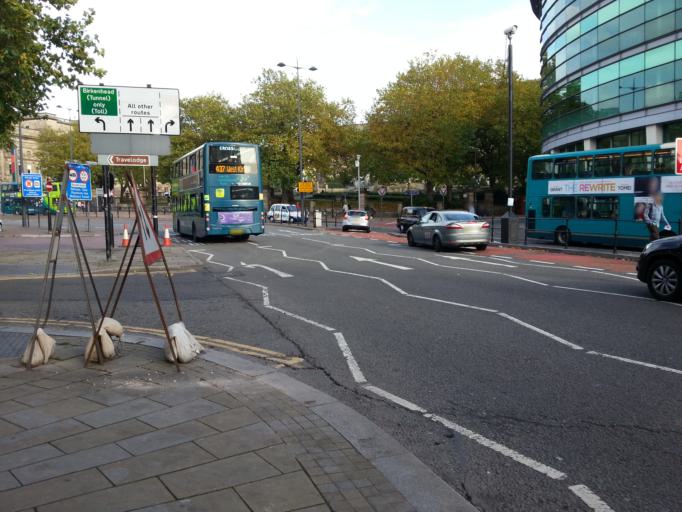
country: GB
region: England
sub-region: Liverpool
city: Liverpool
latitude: 53.4087
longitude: -2.9832
